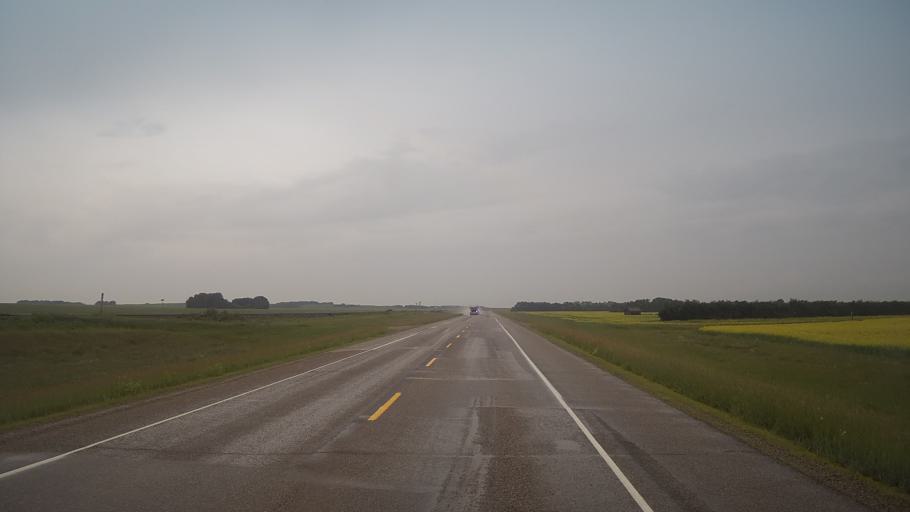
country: CA
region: Saskatchewan
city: Wilkie
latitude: 52.2341
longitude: -108.5490
